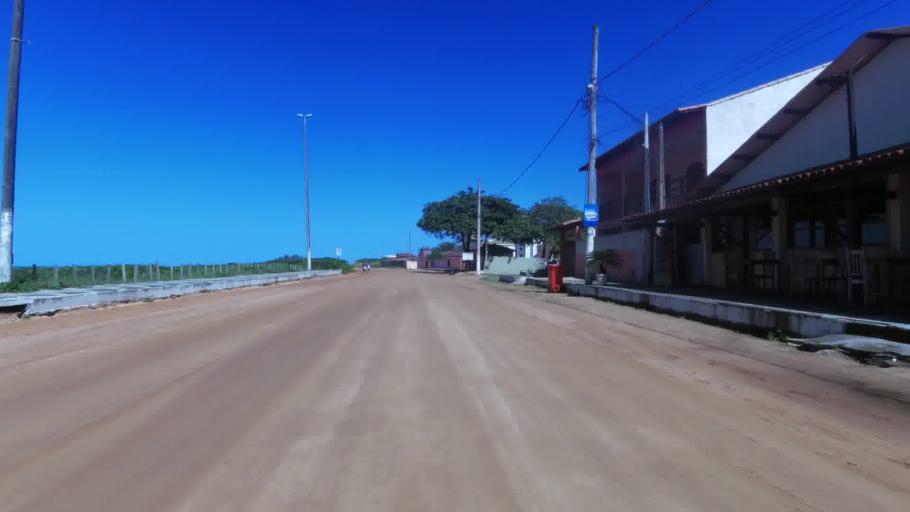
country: BR
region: Espirito Santo
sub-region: Piuma
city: Piuma
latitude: -20.8363
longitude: -40.6267
